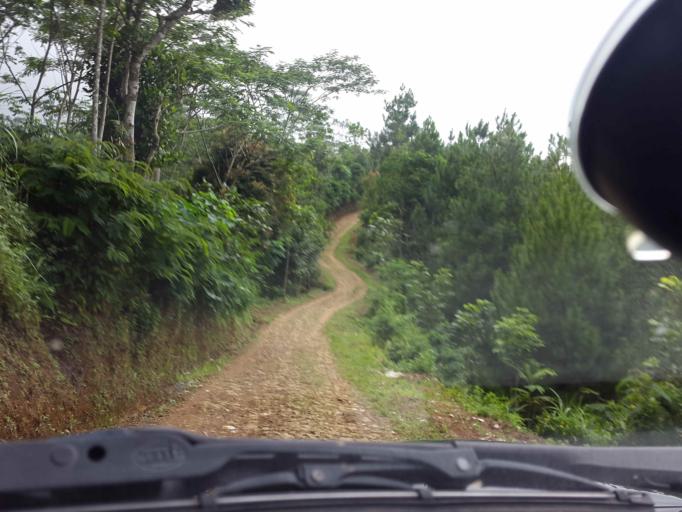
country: ID
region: Central Java
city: Wonosobo
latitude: -7.4739
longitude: 109.9256
